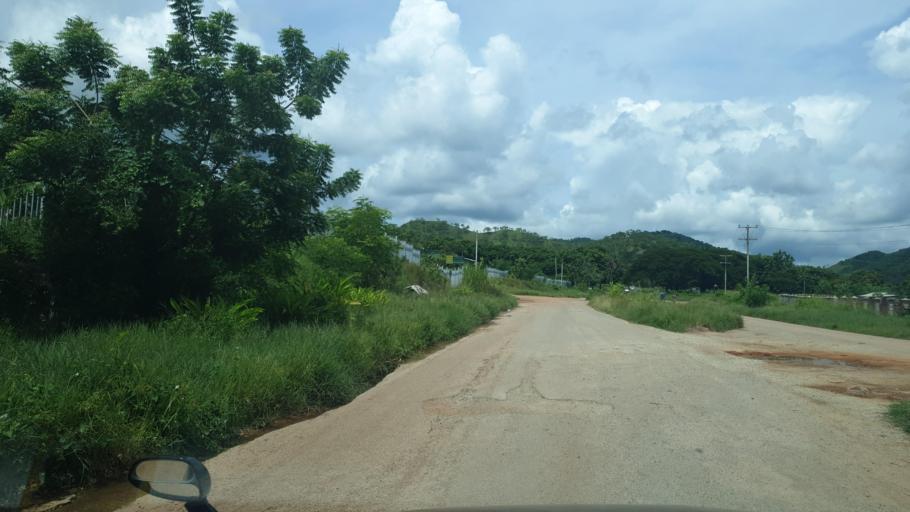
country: PG
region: National Capital
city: Port Moresby
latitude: -9.3767
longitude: 147.1530
